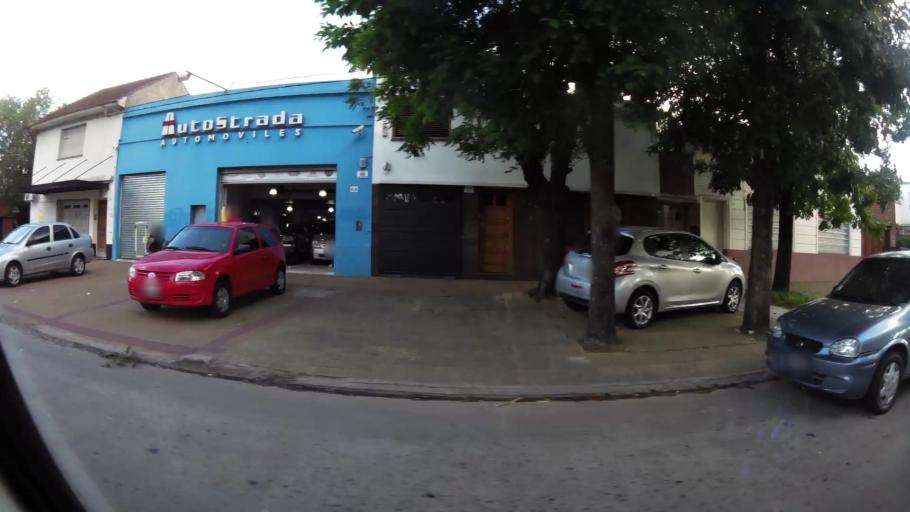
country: AR
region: Buenos Aires
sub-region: Partido de La Plata
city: La Plata
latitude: -34.8935
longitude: -57.9605
